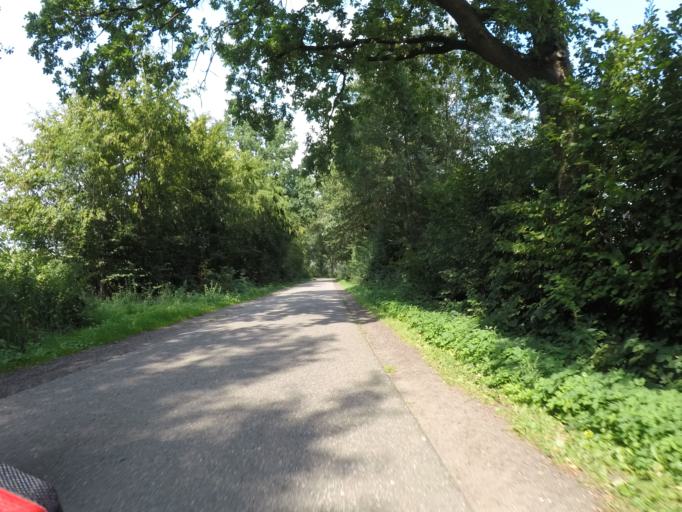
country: DE
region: Schleswig-Holstein
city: Kisdorf
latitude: 53.7784
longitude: 10.0289
